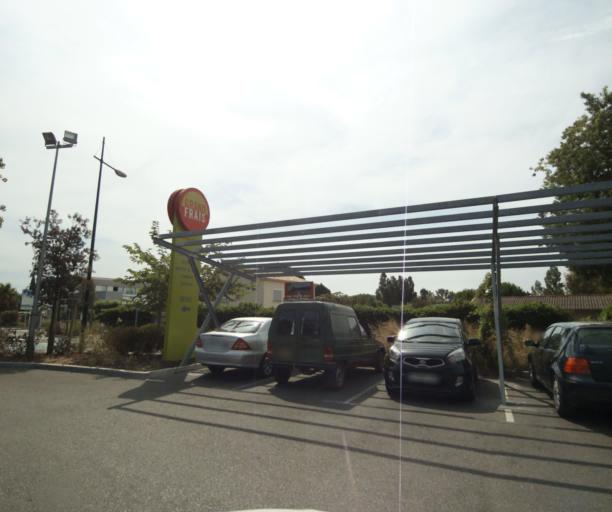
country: FR
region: Provence-Alpes-Cote d'Azur
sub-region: Departement du Var
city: La Garde
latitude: 43.1342
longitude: 6.0295
